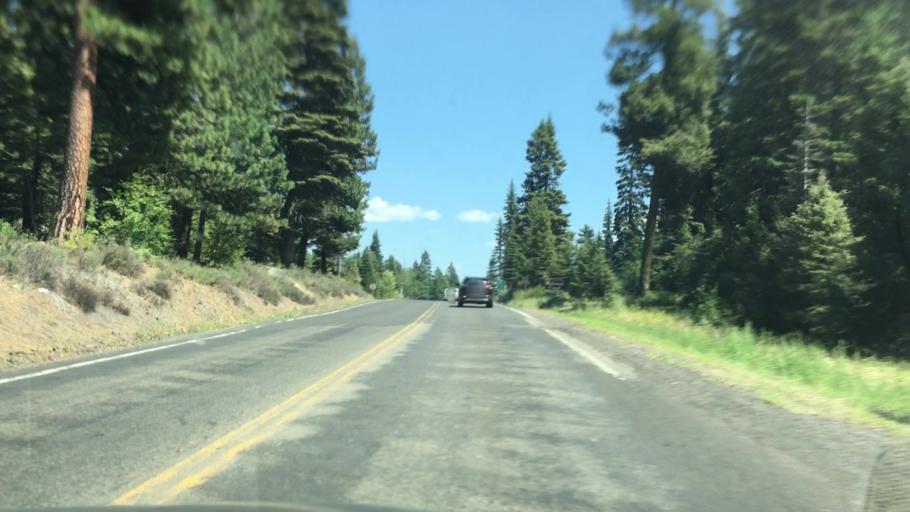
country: US
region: Idaho
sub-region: Valley County
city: McCall
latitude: 44.9297
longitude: -116.1571
